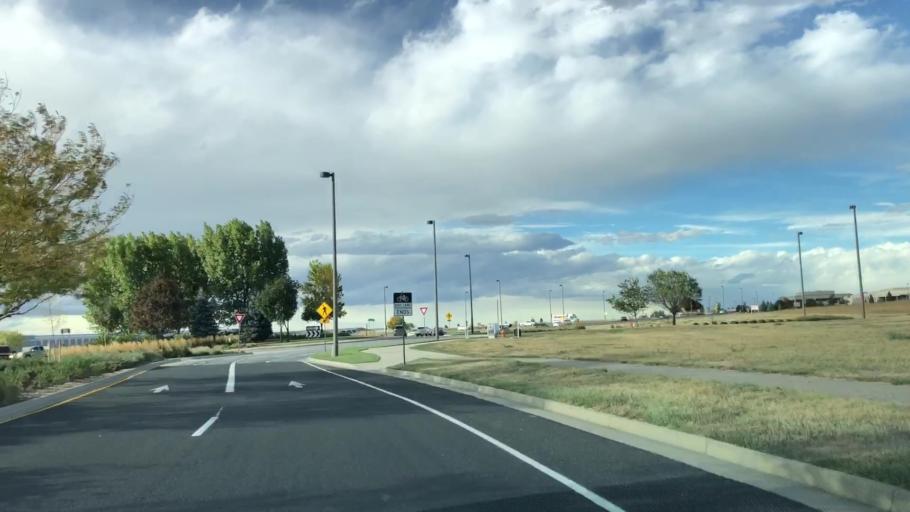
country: US
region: Colorado
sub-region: Larimer County
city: Loveland
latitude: 40.4253
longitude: -105.0020
